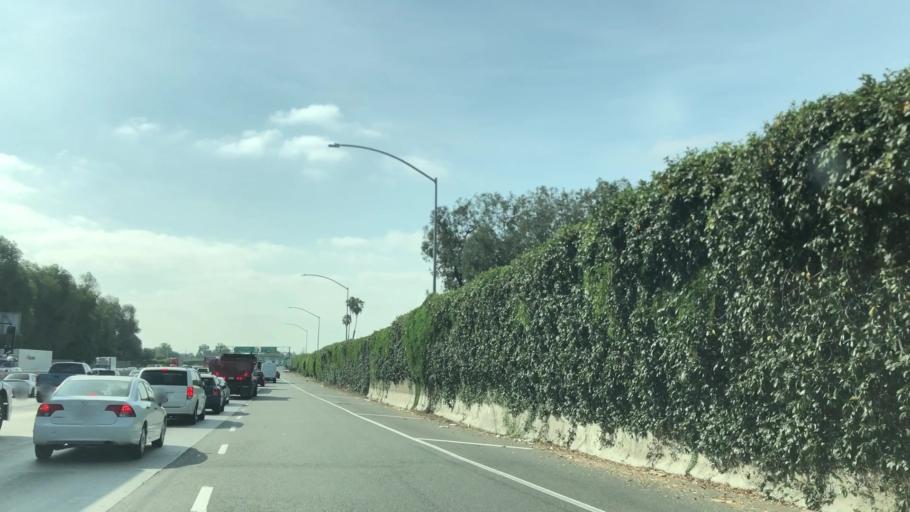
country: US
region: California
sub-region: Los Angeles County
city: Santa Fe Springs
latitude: 33.9561
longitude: -118.1099
